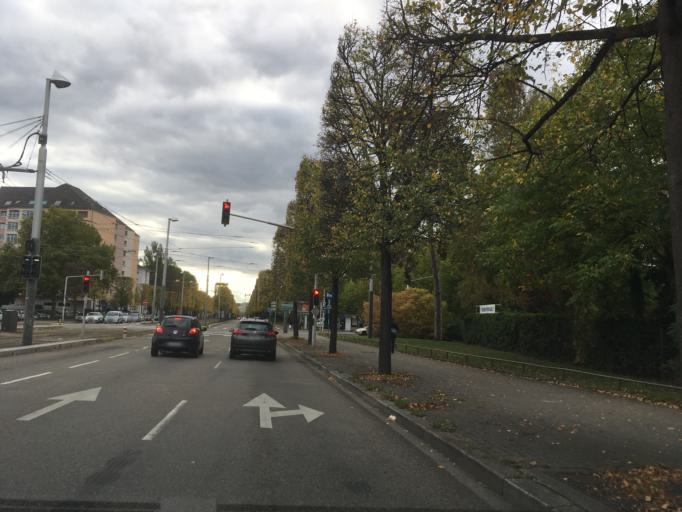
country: FR
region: Alsace
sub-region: Departement du Bas-Rhin
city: Strasbourg
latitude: 48.5619
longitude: 7.7520
